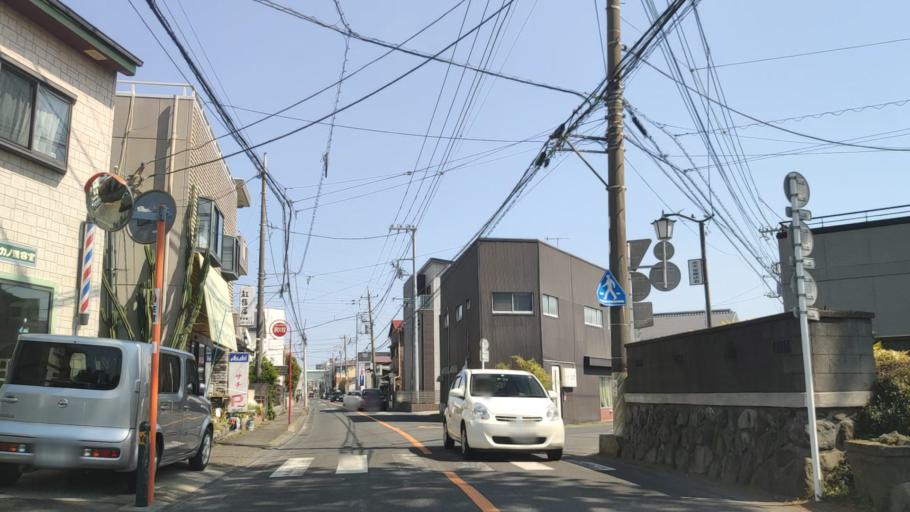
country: JP
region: Kanagawa
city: Hiratsuka
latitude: 35.3376
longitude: 139.3324
